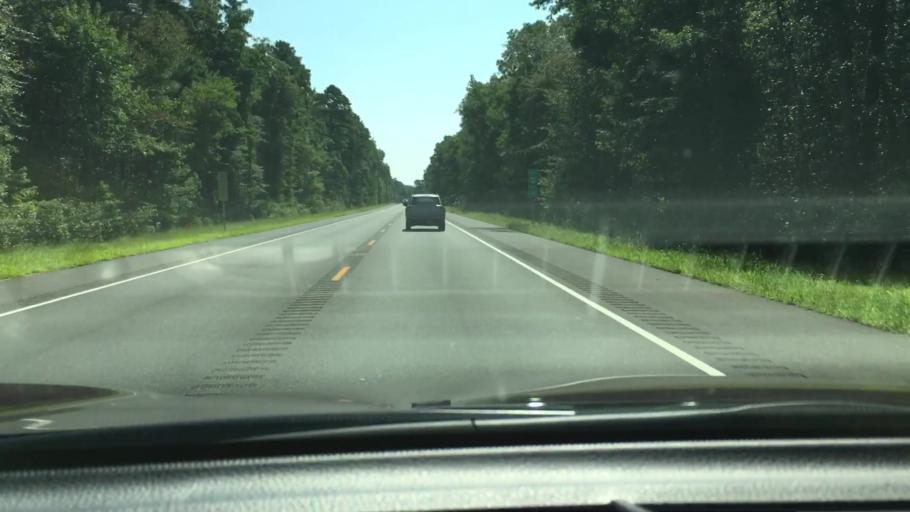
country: US
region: New Jersey
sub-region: Cape May County
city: Woodbine
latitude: 39.3148
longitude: -74.8312
